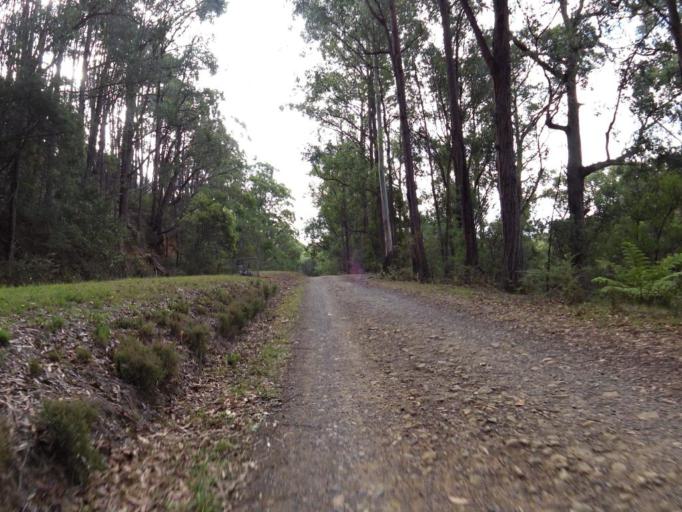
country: AU
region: Victoria
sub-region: Yarra Ranges
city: Mount Evelyn
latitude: -37.8066
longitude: 145.3931
